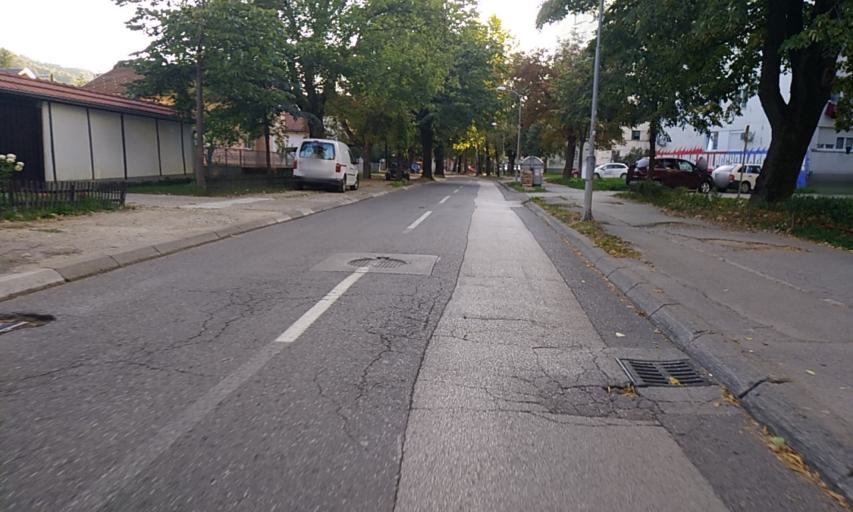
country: BA
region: Republika Srpska
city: Mejdan - Obilicevo
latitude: 44.7608
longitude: 17.1866
